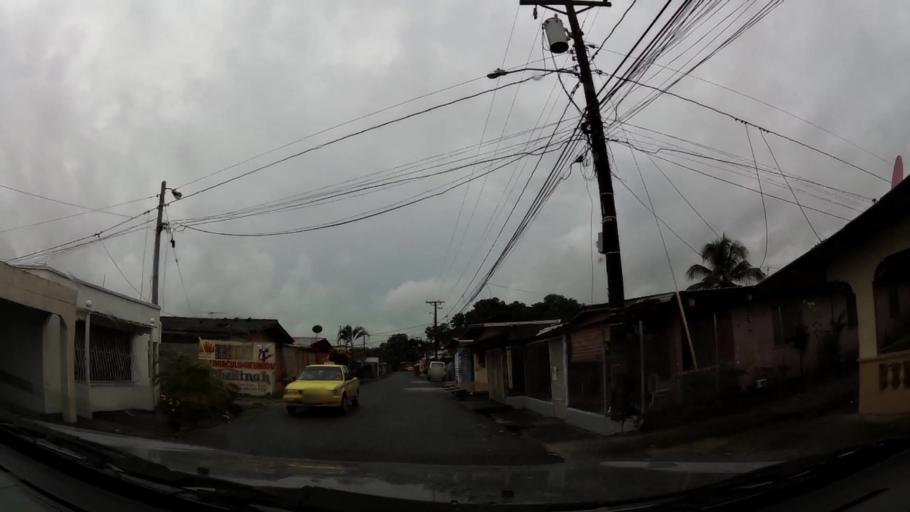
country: PA
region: Colon
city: Arco Iris
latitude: 9.3386
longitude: -79.8767
